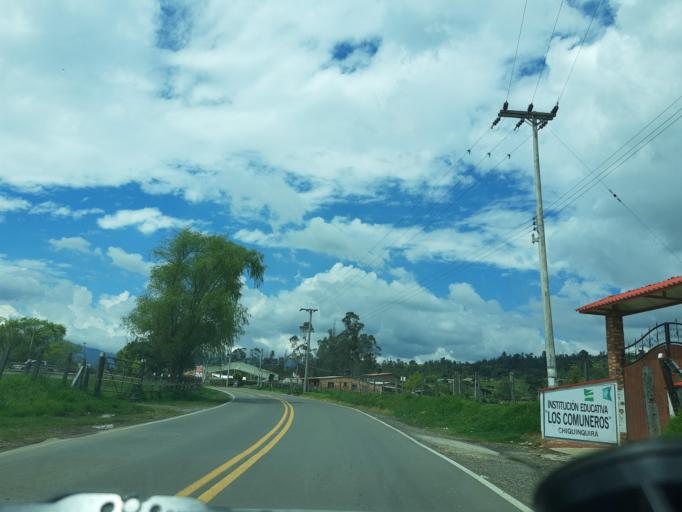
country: CO
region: Boyaca
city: Chiquinquira
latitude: 5.6109
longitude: -73.7382
